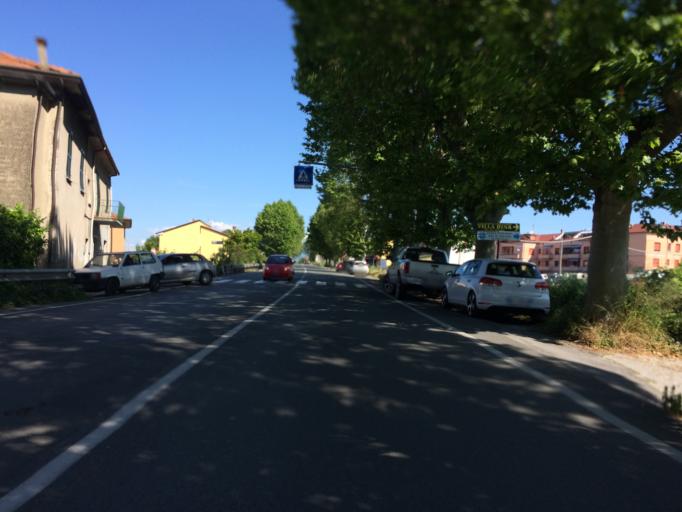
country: IT
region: Liguria
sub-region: Provincia di La Spezia
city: Colombiera-Molicciara
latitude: 44.0799
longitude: 10.0107
